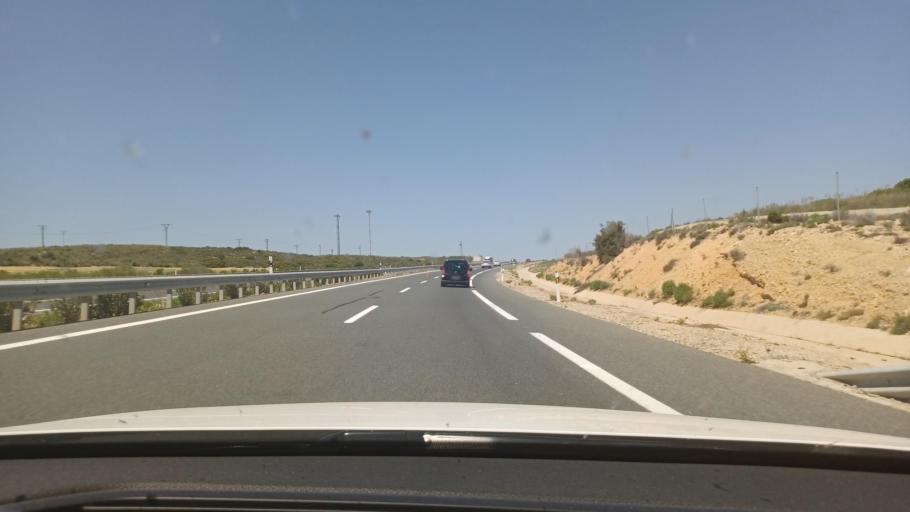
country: ES
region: Castille-La Mancha
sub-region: Provincia de Albacete
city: Alpera
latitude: 38.8783
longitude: -1.1947
